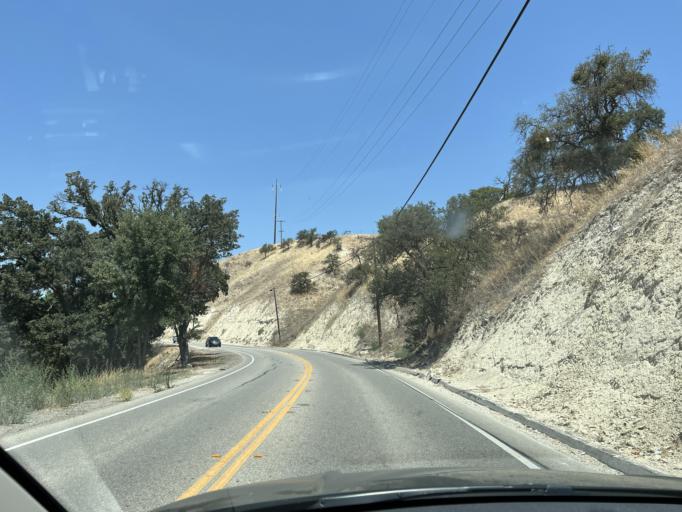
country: US
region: California
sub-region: San Luis Obispo County
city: Paso Robles
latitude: 35.6233
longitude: -120.6803
